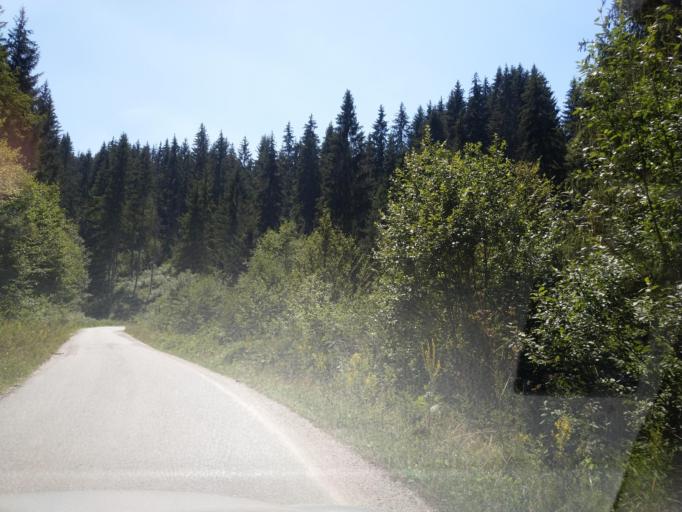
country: RS
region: Central Serbia
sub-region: Zlatiborski Okrug
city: Nova Varos
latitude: 43.4800
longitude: 19.9723
